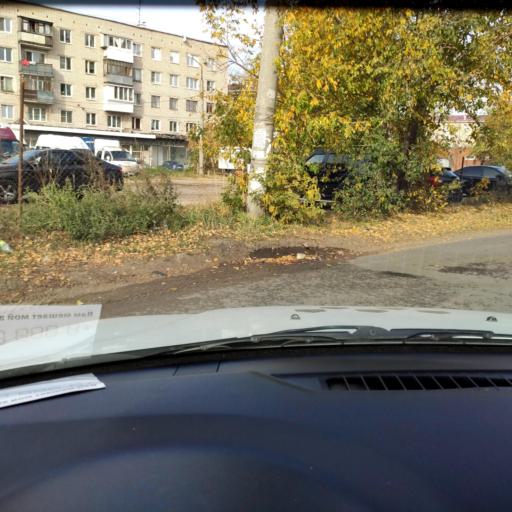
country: RU
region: Samara
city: Tol'yatti
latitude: 53.5307
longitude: 49.4255
